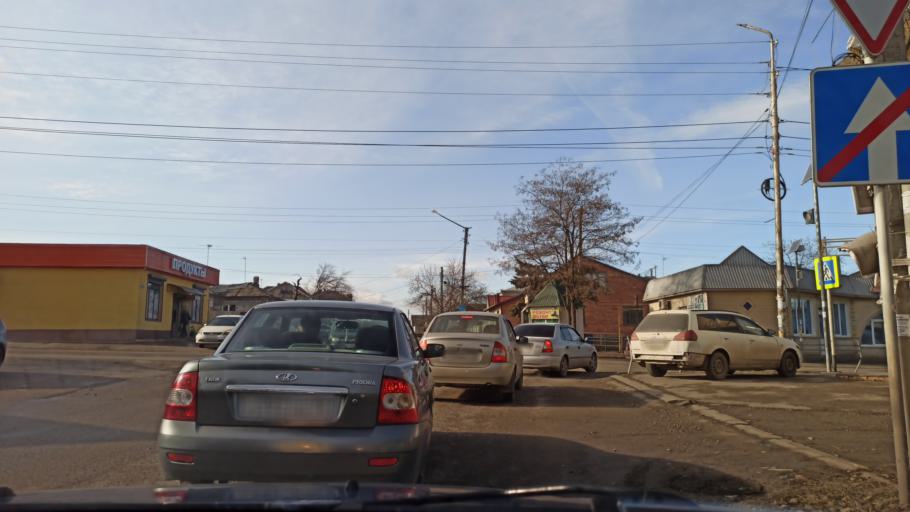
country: RU
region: Stavropol'skiy
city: Yessentuki
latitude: 44.0268
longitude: 42.8612
